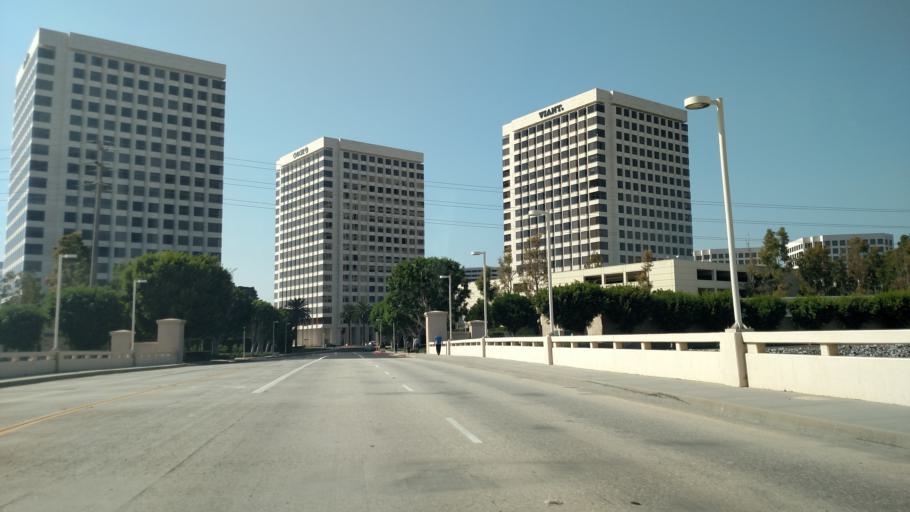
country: US
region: California
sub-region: Orange County
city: Irvine
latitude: 33.6773
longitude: -117.8350
